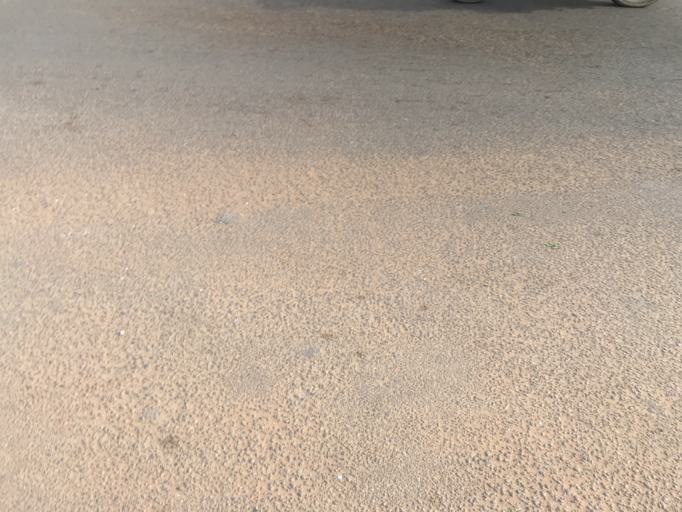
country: NE
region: Niamey
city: Niamey
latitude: 13.5083
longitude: 2.1150
